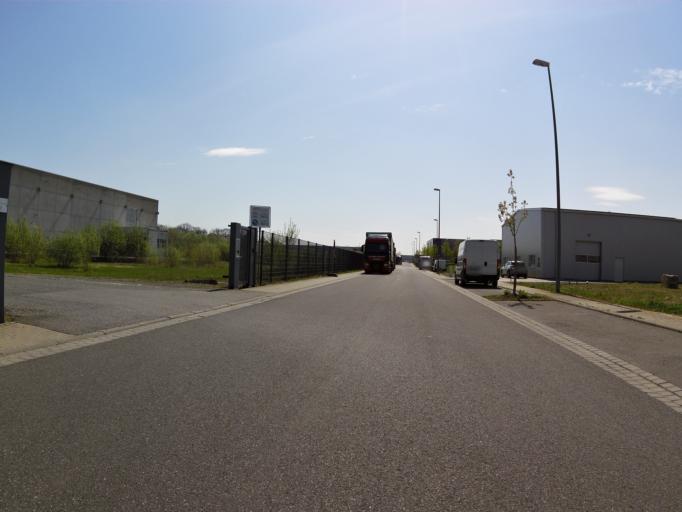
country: DE
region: Bavaria
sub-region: Regierungsbezirk Unterfranken
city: Giebelstadt
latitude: 49.6937
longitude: 9.9433
